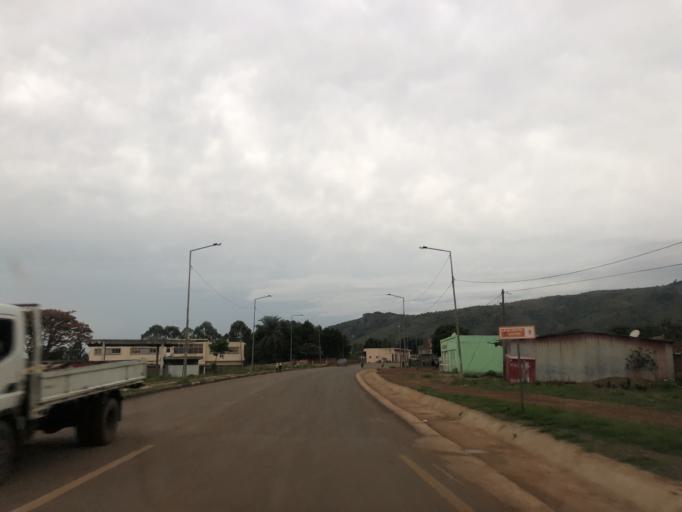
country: AO
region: Cuanza Sul
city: Uacu Cungo
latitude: -11.3552
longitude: 15.1214
